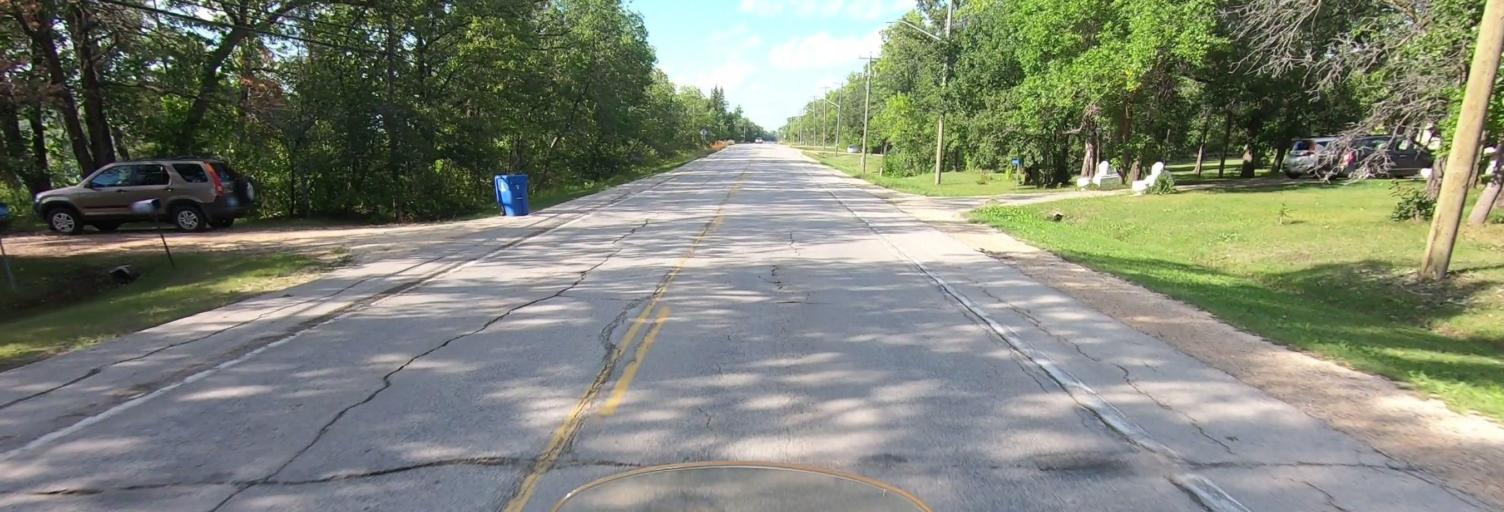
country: CA
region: Manitoba
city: Winnipeg
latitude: 49.9964
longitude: -97.0373
